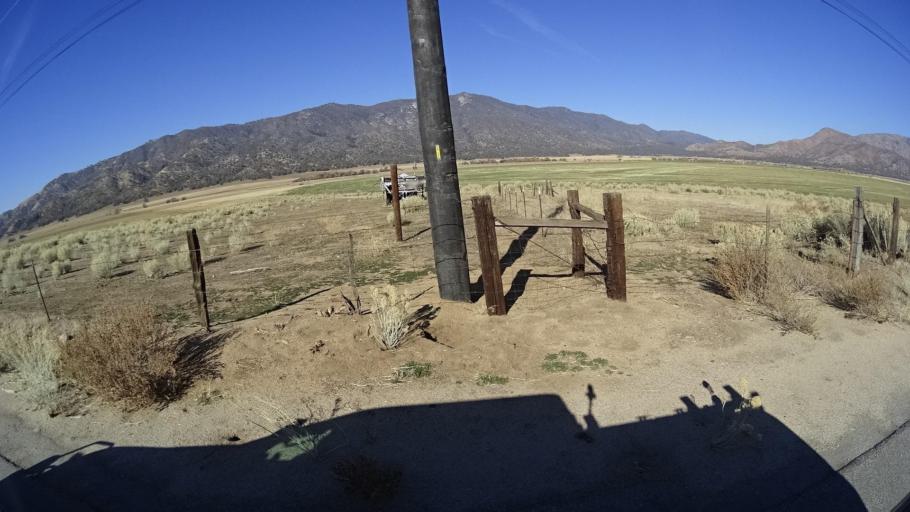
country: US
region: California
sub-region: Kern County
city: Bodfish
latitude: 35.3941
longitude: -118.5269
